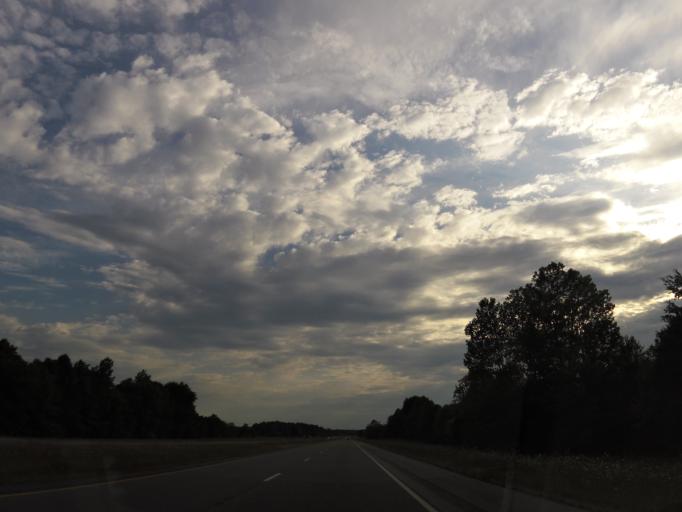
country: US
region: Alabama
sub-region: Lawrence County
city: Moulton
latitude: 34.5010
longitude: -87.2402
